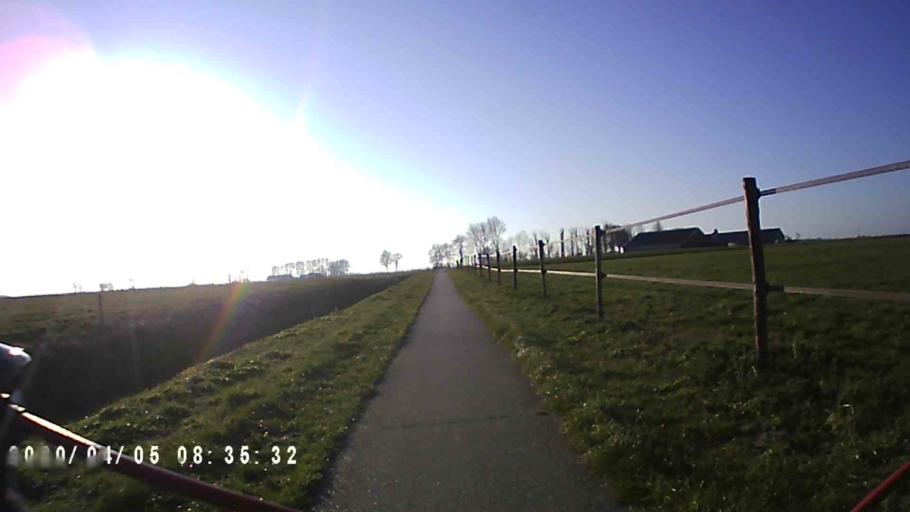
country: NL
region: Groningen
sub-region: Gemeente Winsum
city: Winsum
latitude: 53.3222
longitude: 6.4968
